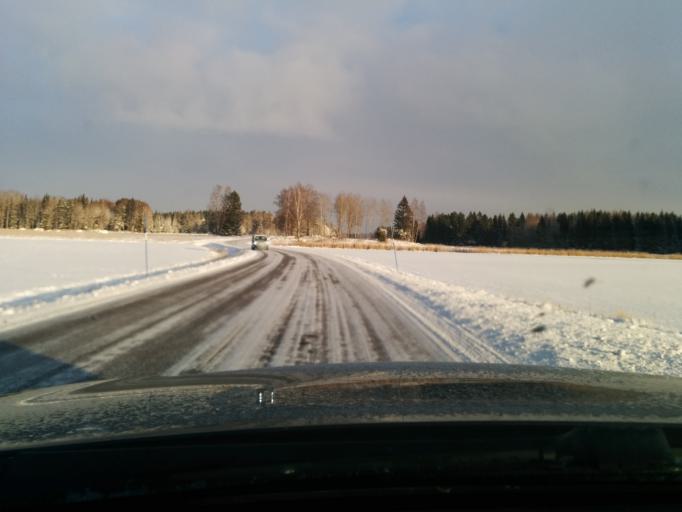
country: SE
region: Uppsala
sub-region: Tierps Kommun
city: Orbyhus
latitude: 60.1865
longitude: 17.6742
